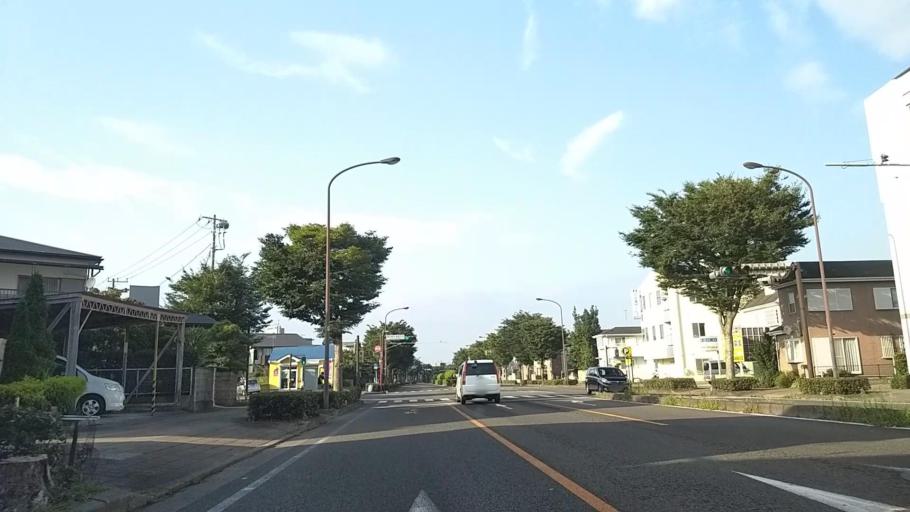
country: JP
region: Kanagawa
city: Hiratsuka
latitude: 35.3268
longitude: 139.3326
